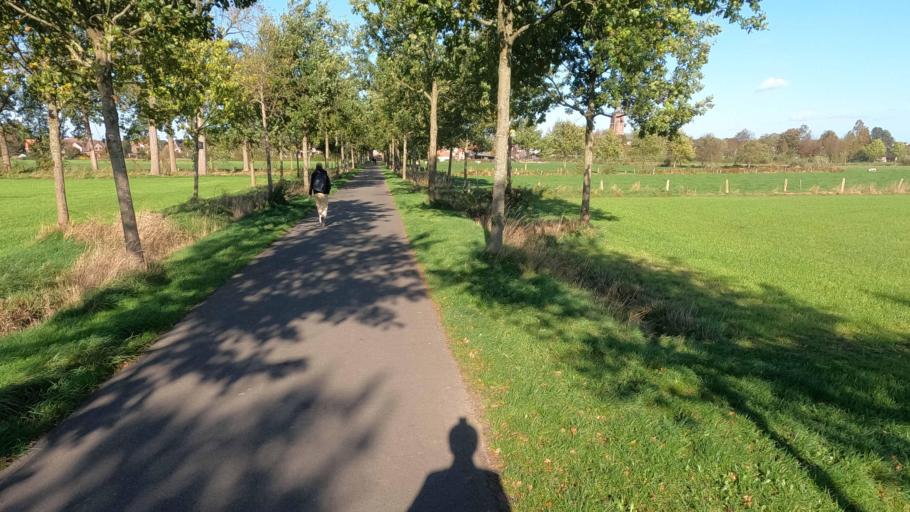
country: BE
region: Flanders
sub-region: Provincie Antwerpen
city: Wuustwezel
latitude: 51.3843
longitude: 4.5966
